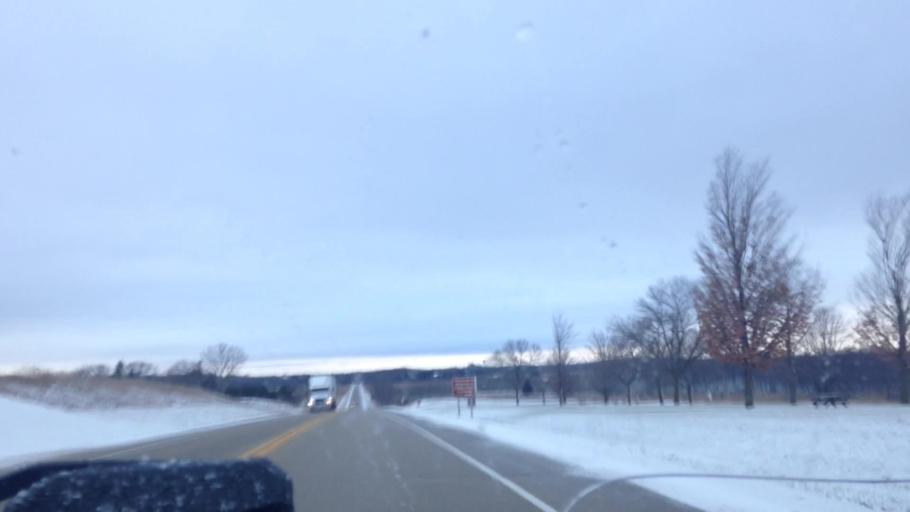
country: US
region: Wisconsin
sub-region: Dodge County
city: Horicon
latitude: 43.4735
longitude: -88.5985
